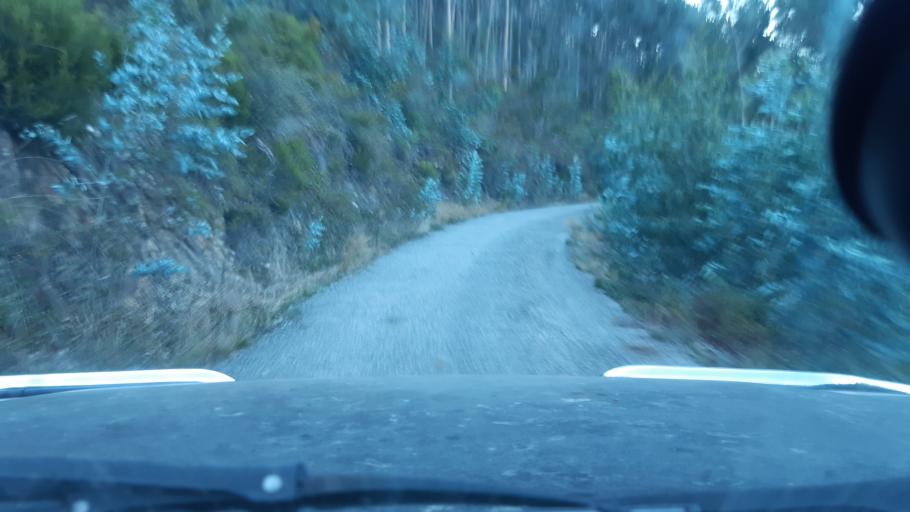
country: PT
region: Viseu
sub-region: Mortagua
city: Mortagua
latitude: 40.5214
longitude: -8.2522
